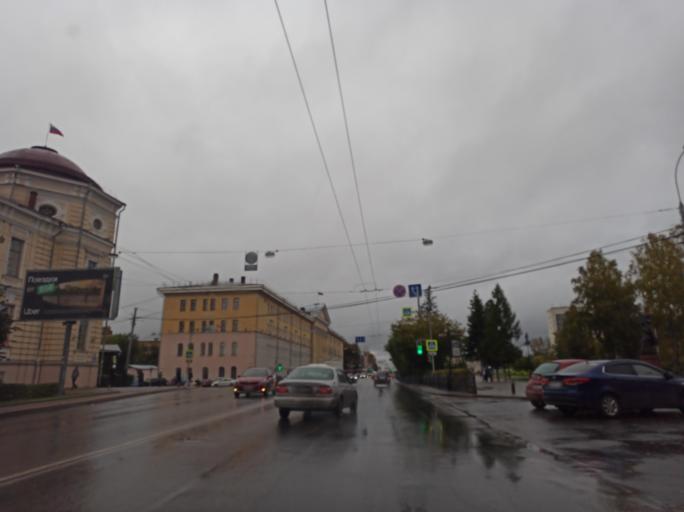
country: RU
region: Tomsk
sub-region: Tomskiy Rayon
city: Tomsk
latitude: 56.4725
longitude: 84.9505
